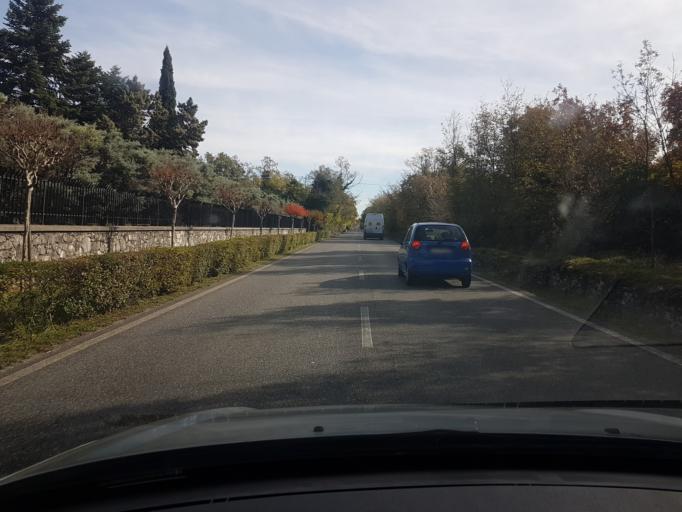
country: IT
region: Friuli Venezia Giulia
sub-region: Provincia di Trieste
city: Santa Croce
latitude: 45.7305
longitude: 13.7038
